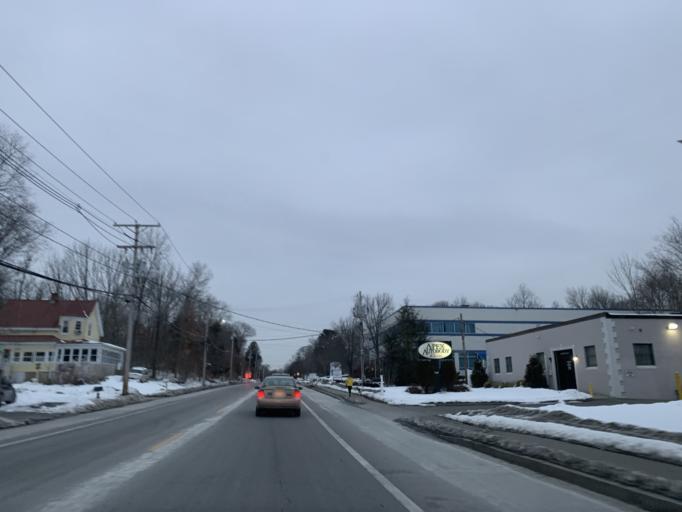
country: US
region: Massachusetts
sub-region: Norfolk County
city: Avon
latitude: 42.1042
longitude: -71.0686
